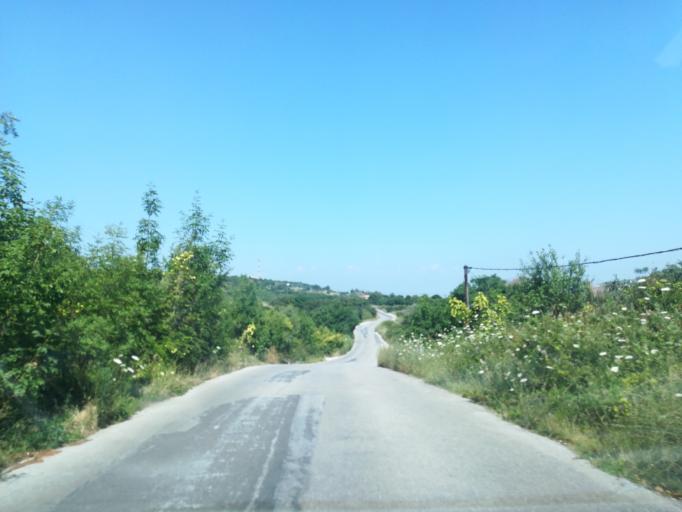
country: GR
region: Central Macedonia
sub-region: Nomos Thessalonikis
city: Asvestochori
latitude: 40.6312
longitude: 23.0299
